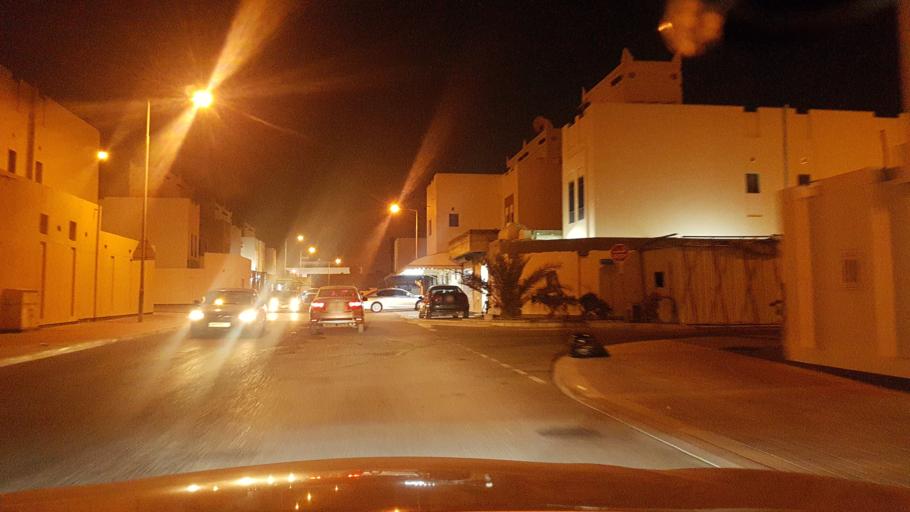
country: BH
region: Central Governorate
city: Madinat Hamad
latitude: 26.0948
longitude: 50.4845
